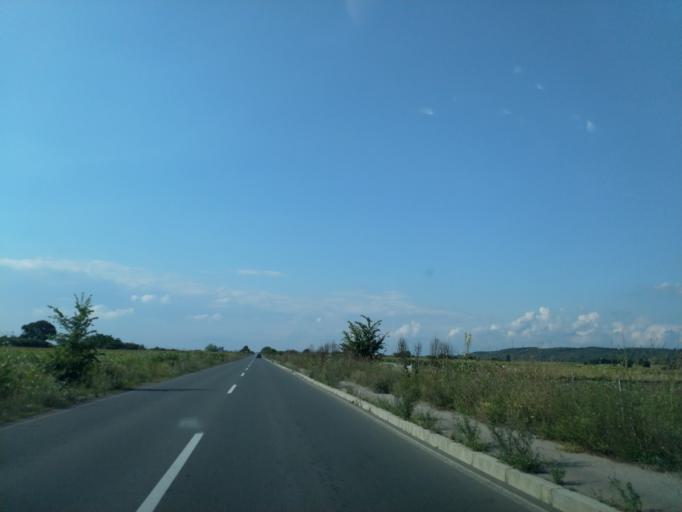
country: RS
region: Central Serbia
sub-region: Pomoravski Okrug
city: Paracin
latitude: 43.8118
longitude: 21.4202
